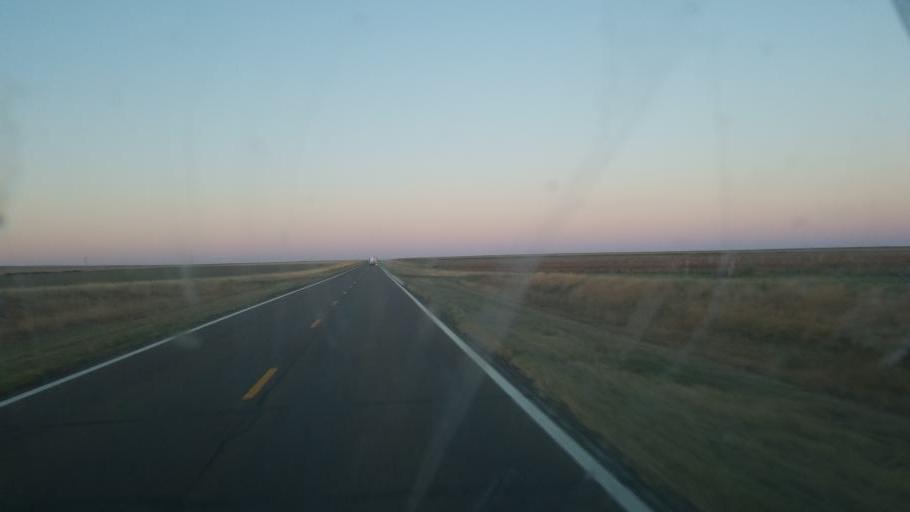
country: US
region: Kansas
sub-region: Wallace County
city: Sharon Springs
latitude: 38.9047
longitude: -101.6342
